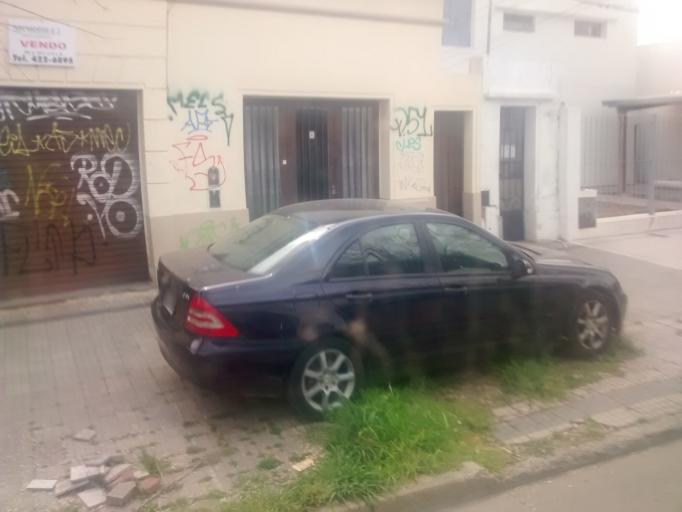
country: AR
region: Buenos Aires
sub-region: Partido de La Plata
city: La Plata
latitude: -34.9317
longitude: -57.9350
